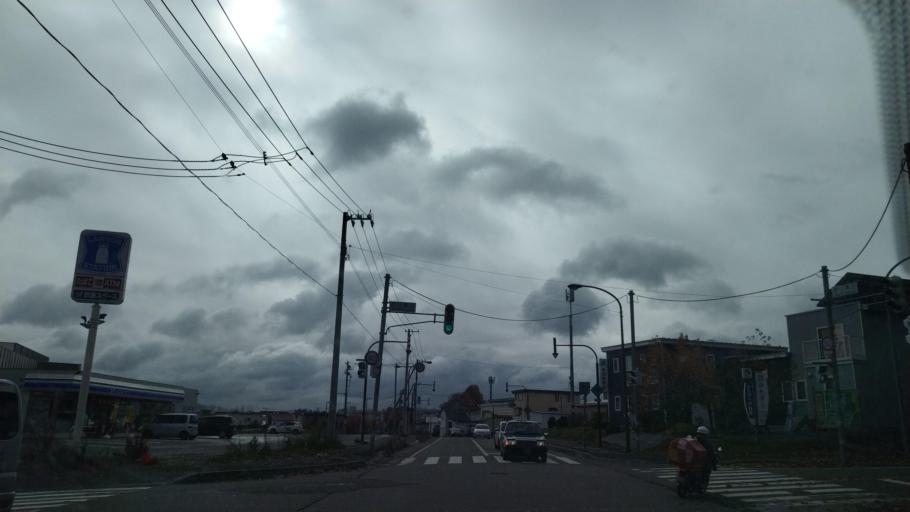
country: JP
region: Hokkaido
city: Obihiro
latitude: 42.8860
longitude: 143.1902
